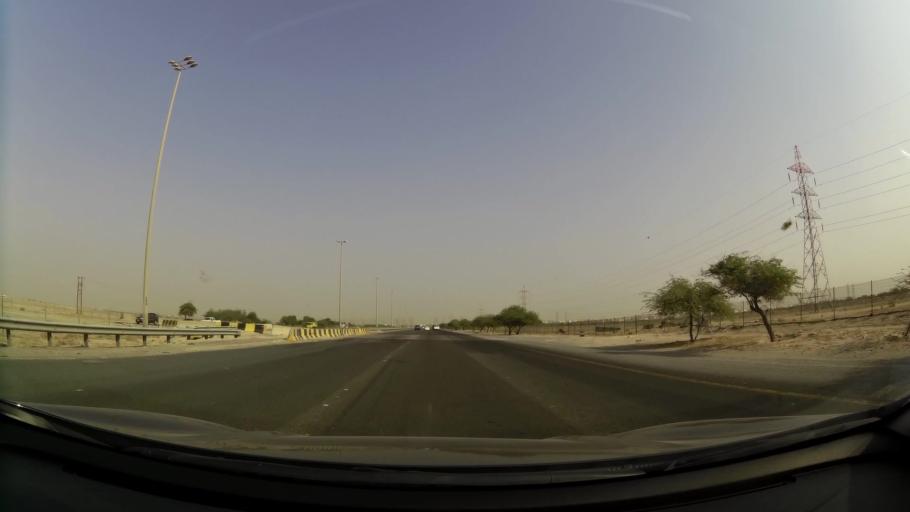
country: KW
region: Al Asimah
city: Ar Rabiyah
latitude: 29.2188
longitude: 47.8850
